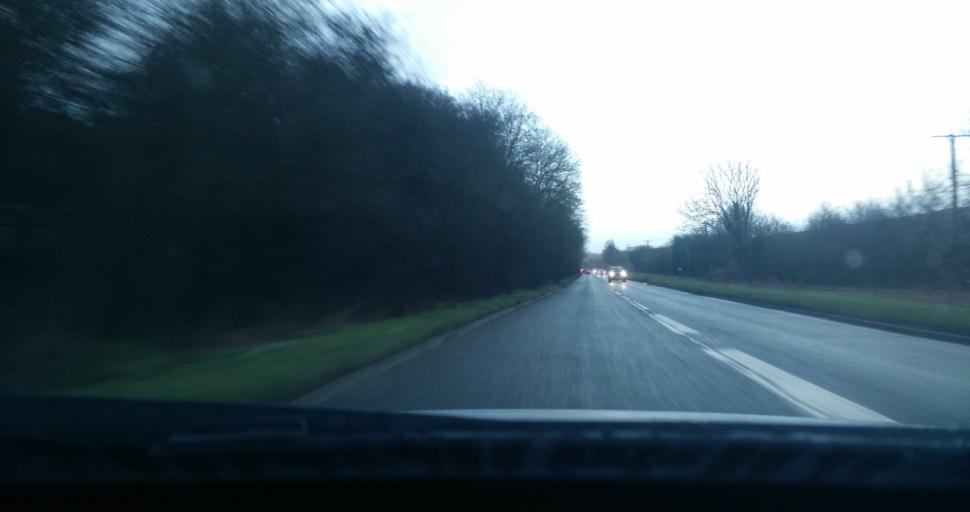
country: GB
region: England
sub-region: Buckinghamshire
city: Amersham
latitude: 51.6576
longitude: -0.6332
